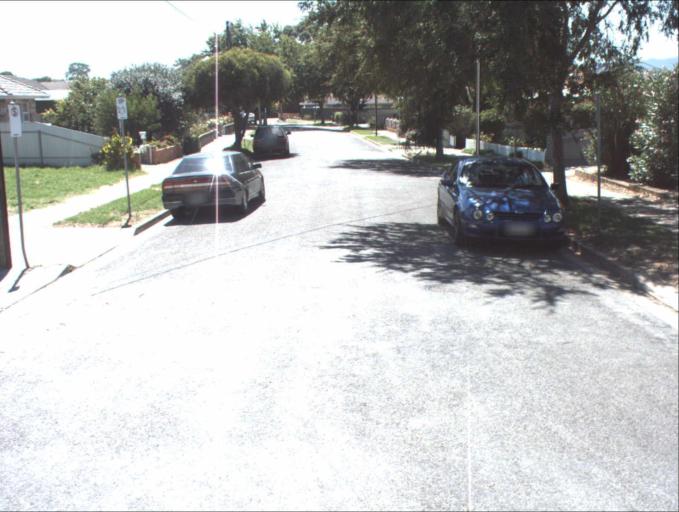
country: AU
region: South Australia
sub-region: Port Adelaide Enfield
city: Klemzig
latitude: -34.8752
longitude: 138.6336
